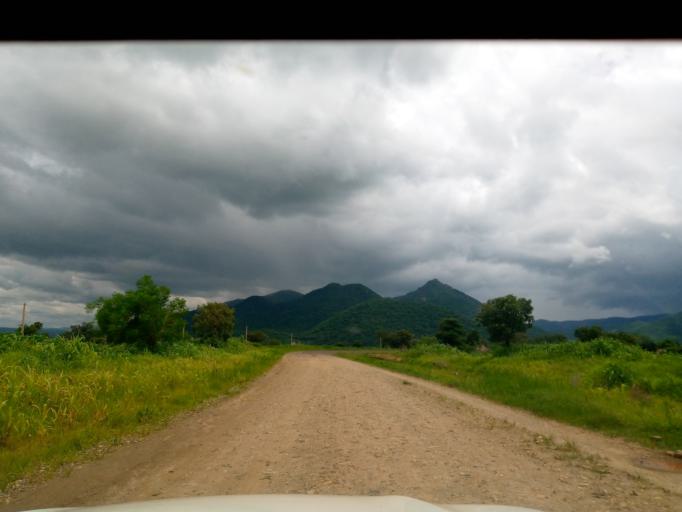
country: ET
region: Oromiya
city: Mendi
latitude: 10.1815
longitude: 35.0925
